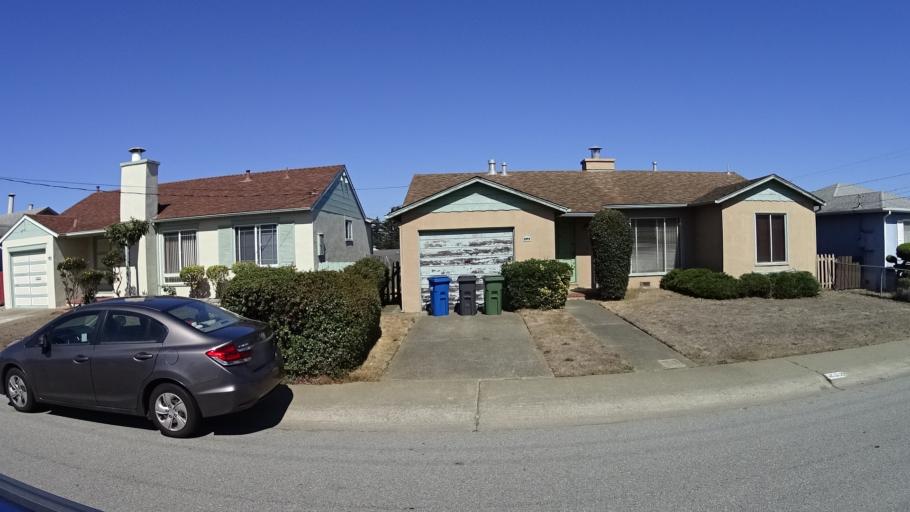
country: US
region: California
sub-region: San Mateo County
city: Broadmoor
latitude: 37.6941
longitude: -122.4825
